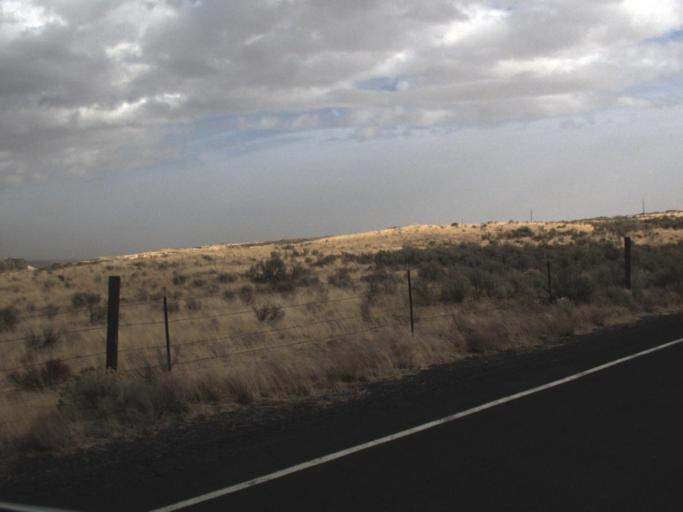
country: US
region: Washington
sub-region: Adams County
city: Ritzville
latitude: 47.4600
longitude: -118.7588
